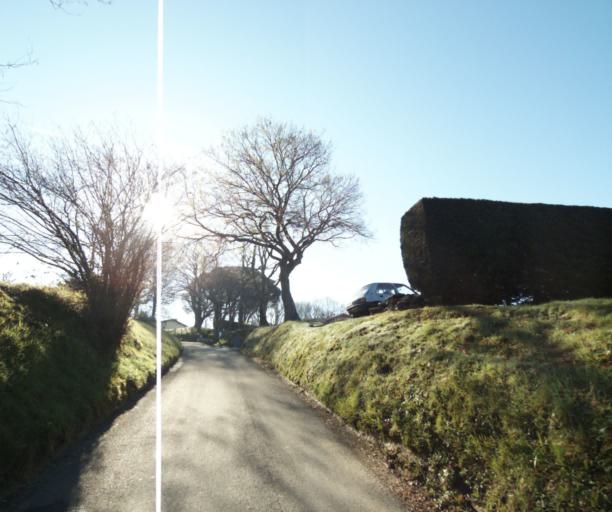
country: FR
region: Aquitaine
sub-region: Departement des Pyrenees-Atlantiques
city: Ciboure
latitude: 43.3669
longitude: -1.6639
